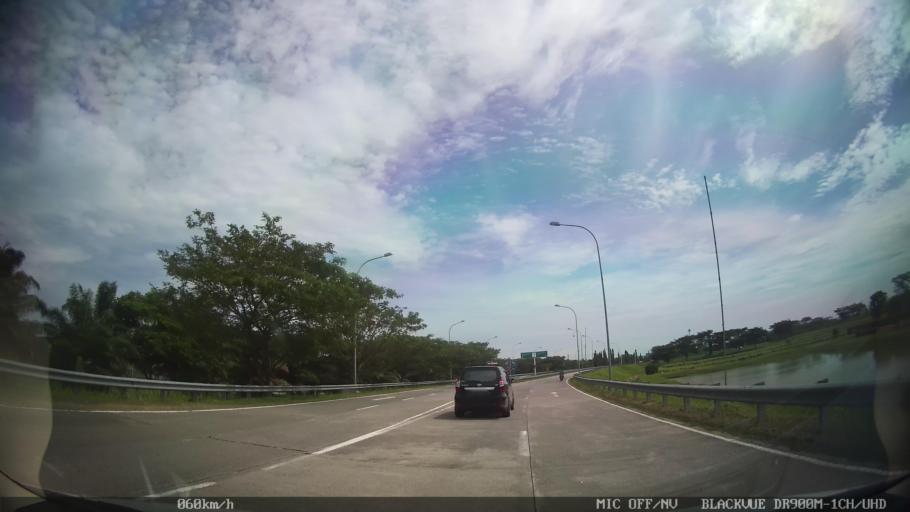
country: ID
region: North Sumatra
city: Percut
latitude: 3.6315
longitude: 98.8734
